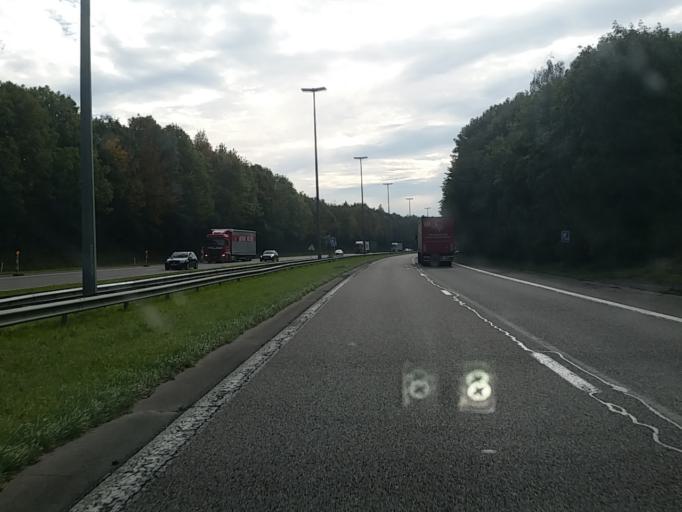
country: BE
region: Wallonia
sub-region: Province du Luxembourg
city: Arlon
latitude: 49.6654
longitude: 5.8075
